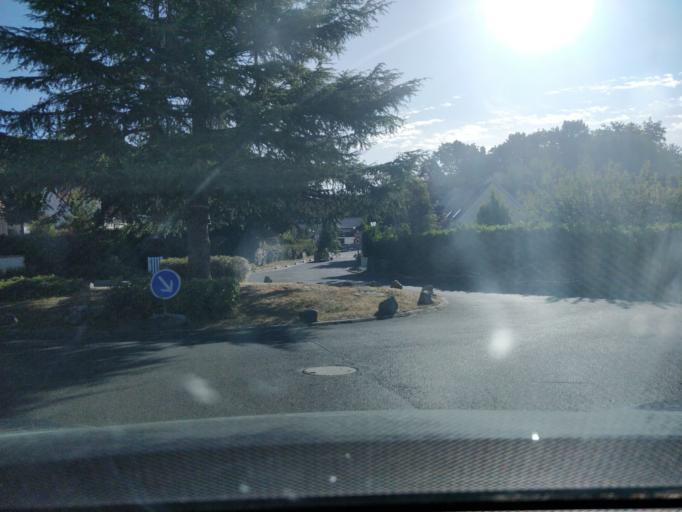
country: FR
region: Ile-de-France
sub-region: Departement de l'Essonne
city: Forges-les-Bains
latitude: 48.6310
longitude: 2.0861
